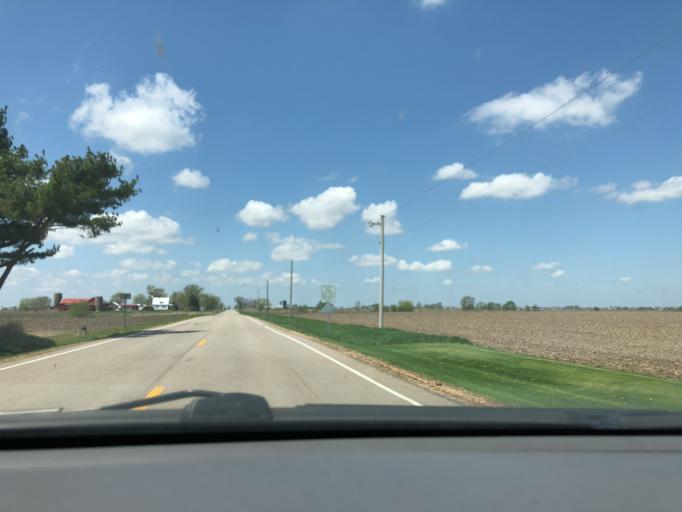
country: US
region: Illinois
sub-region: Kane County
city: Hampshire
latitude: 42.1101
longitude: -88.5689
